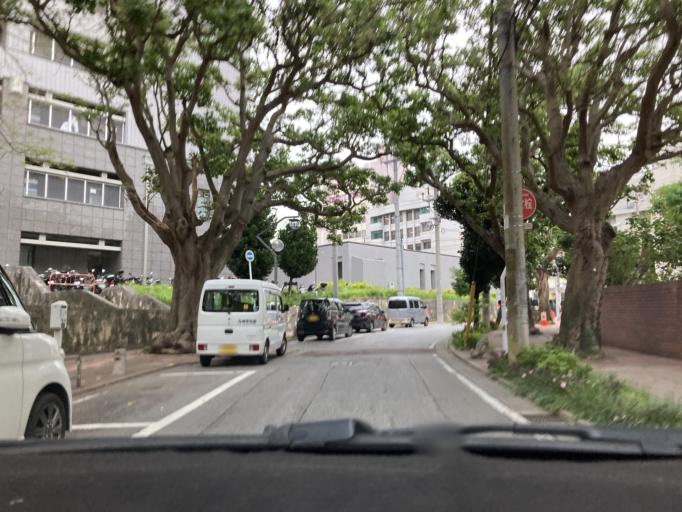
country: JP
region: Okinawa
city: Naha-shi
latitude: 26.2116
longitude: 127.6805
